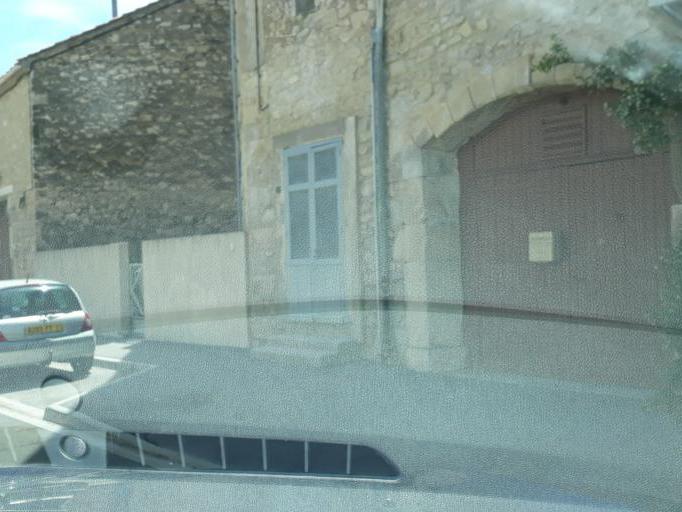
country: FR
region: Languedoc-Roussillon
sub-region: Departement de l'Aude
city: Portel-des-Corbieres
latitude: 43.0523
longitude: 2.9233
